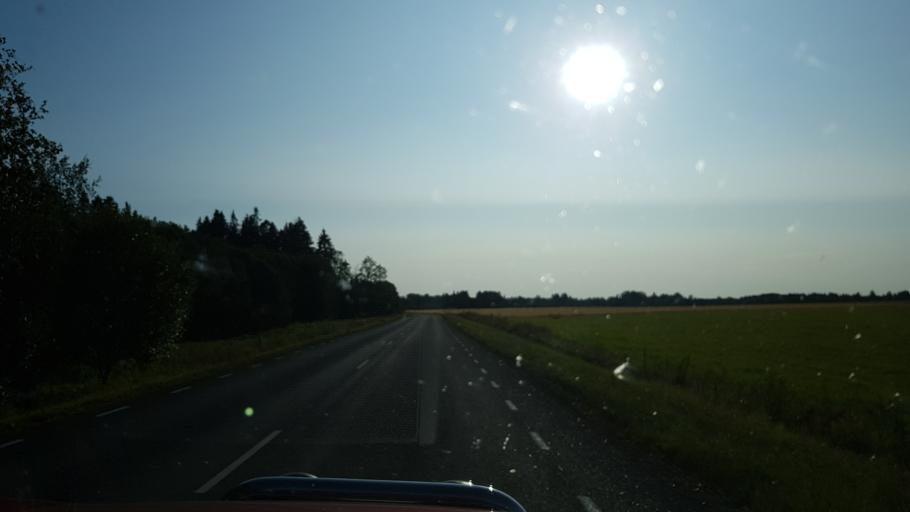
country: EE
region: Raplamaa
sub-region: Kehtna vald
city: Kehtna
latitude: 59.0427
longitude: 25.1002
